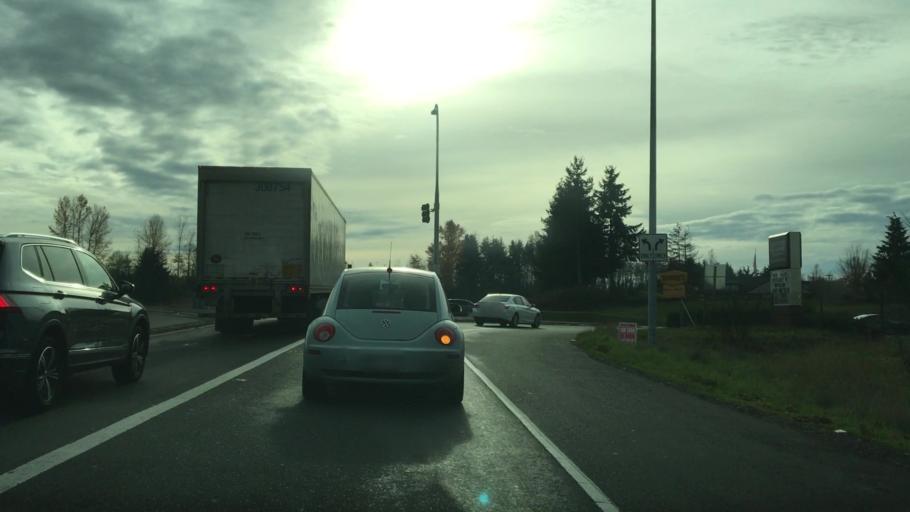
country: US
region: Washington
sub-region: Pierce County
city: Puyallup
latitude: 47.1621
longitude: -122.2985
